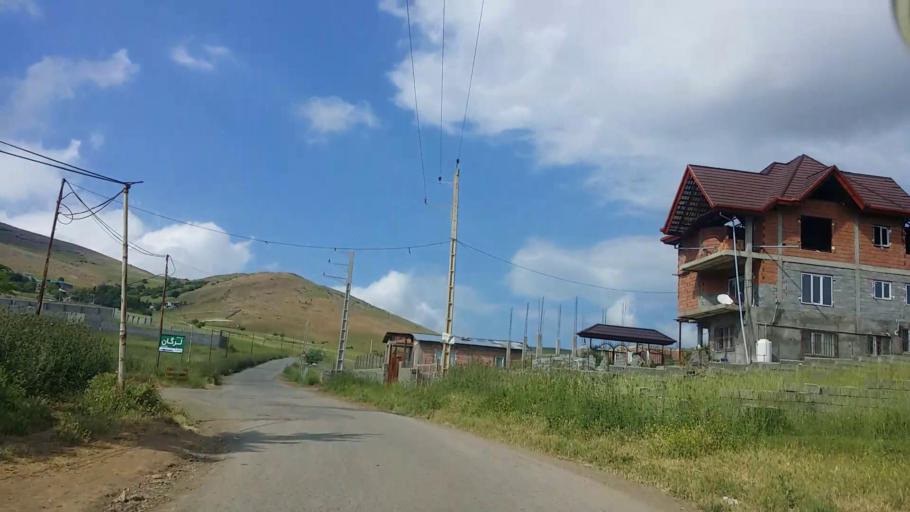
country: IR
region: Mazandaran
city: Chalus
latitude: 36.5217
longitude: 51.2613
